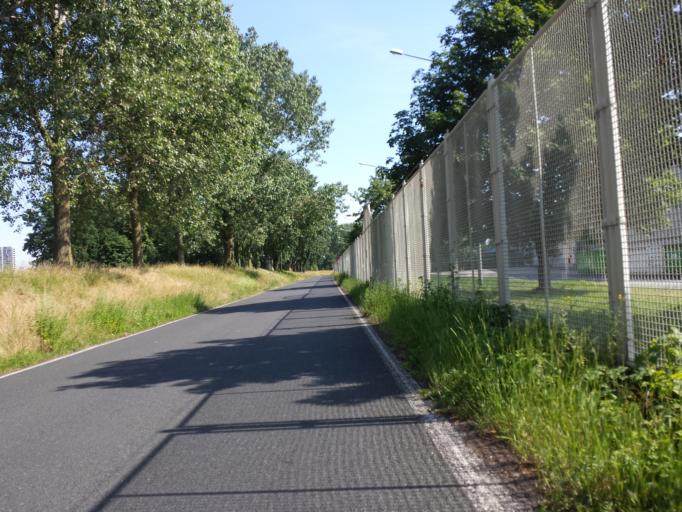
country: DE
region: Bremen
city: Bremen
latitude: 53.1024
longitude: 8.7469
